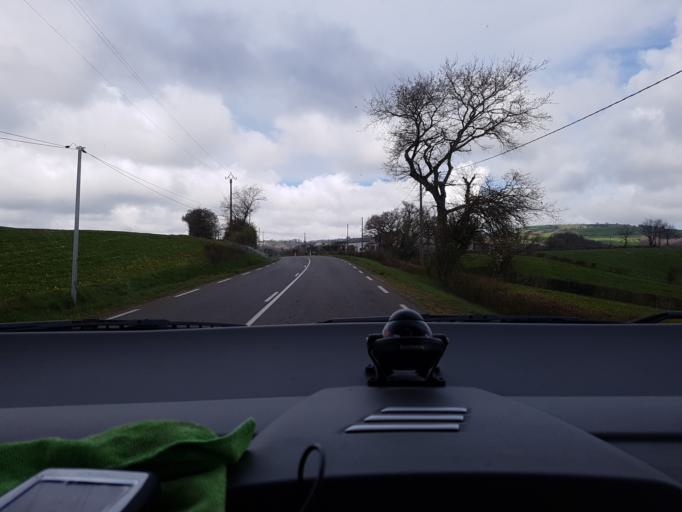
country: FR
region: Midi-Pyrenees
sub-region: Departement de l'Aveyron
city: Moyrazes
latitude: 44.3896
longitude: 2.3964
